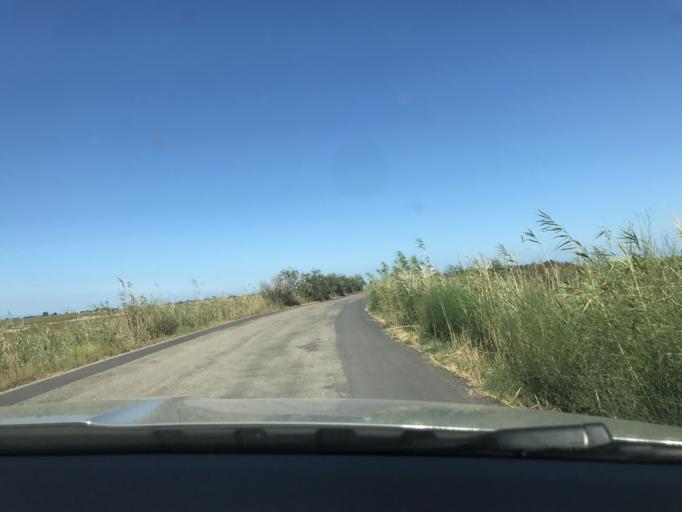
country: ES
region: Catalonia
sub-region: Provincia de Tarragona
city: Deltebre
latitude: 40.6502
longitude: 0.7613
